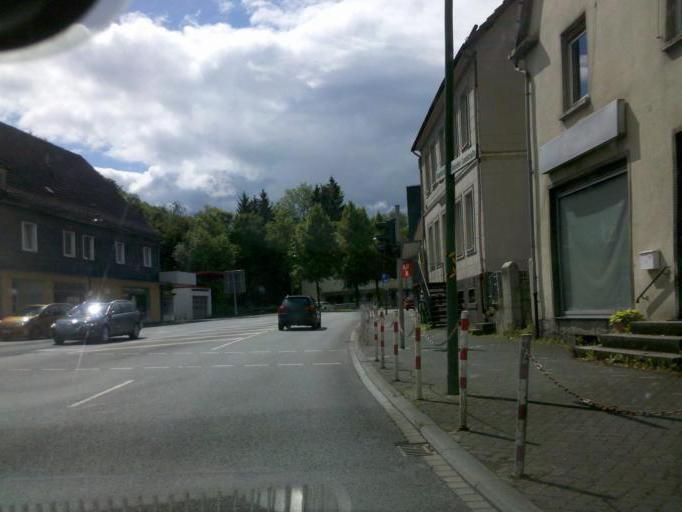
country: DE
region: North Rhine-Westphalia
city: Warstein
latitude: 51.4505
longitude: 8.3555
